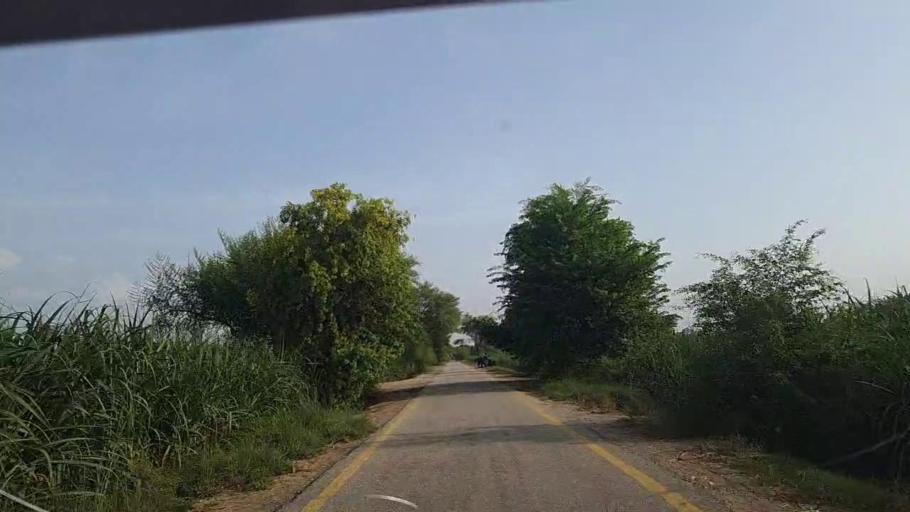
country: PK
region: Sindh
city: Ghotki
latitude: 27.9723
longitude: 69.2559
